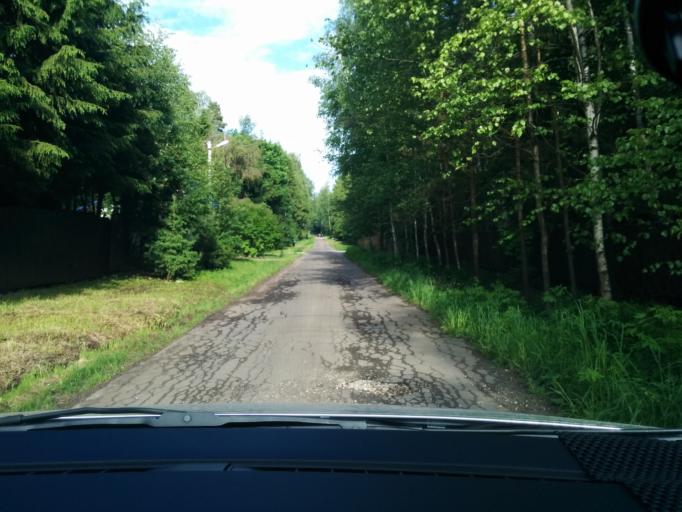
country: RU
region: Moskovskaya
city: Lugovaya
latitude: 56.0606
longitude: 37.4785
